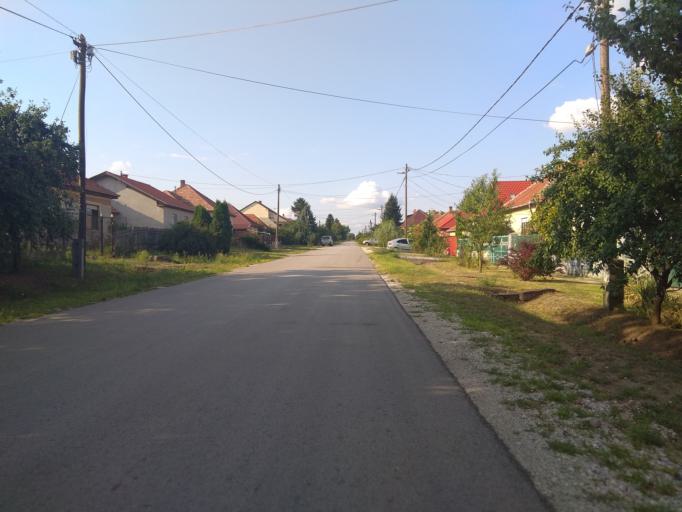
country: HU
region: Borsod-Abauj-Zemplen
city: Emod
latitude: 47.9325
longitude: 20.8077
